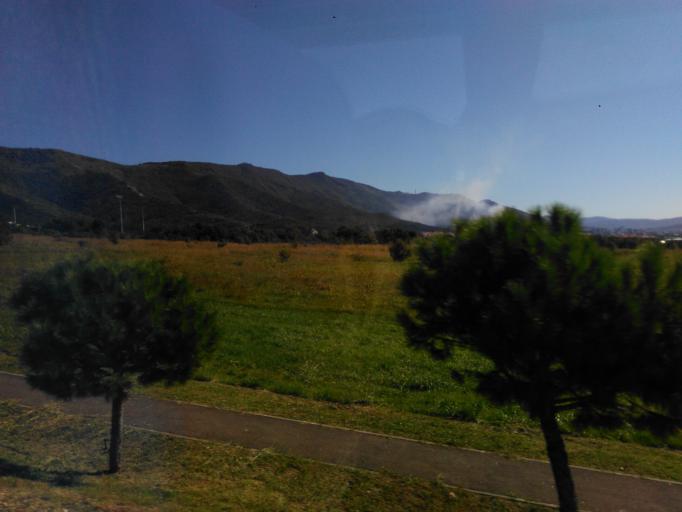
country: RU
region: Krasnodarskiy
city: Gelendzhik
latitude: 44.5958
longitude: 38.0275
